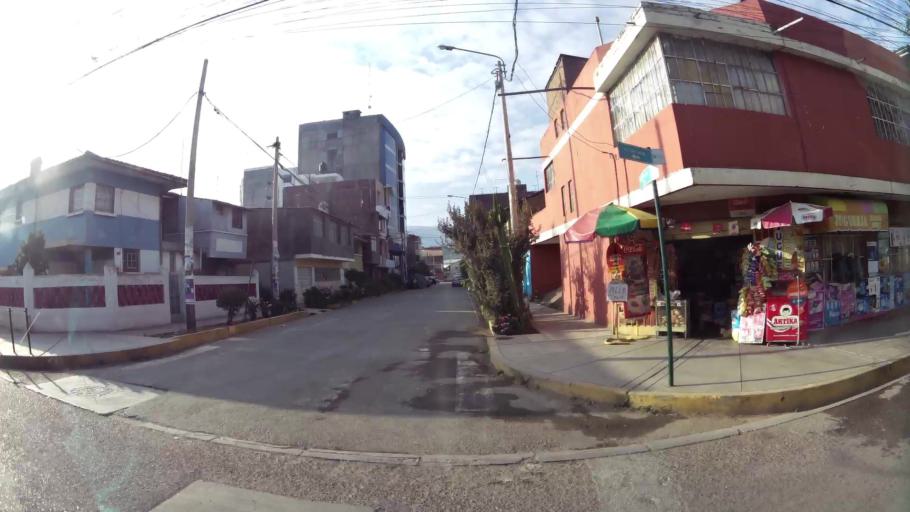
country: PE
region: Junin
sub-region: Provincia de Huancayo
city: Huancayo
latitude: -12.0551
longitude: -75.2036
